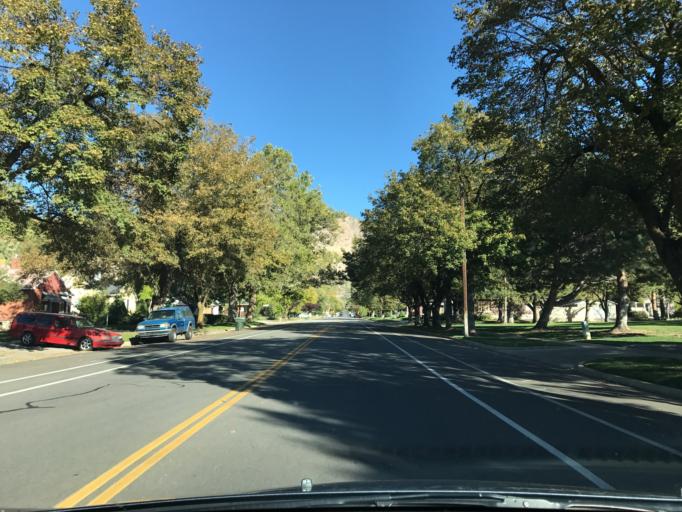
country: US
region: Utah
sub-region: Weber County
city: Ogden
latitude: 41.2183
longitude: -111.9536
